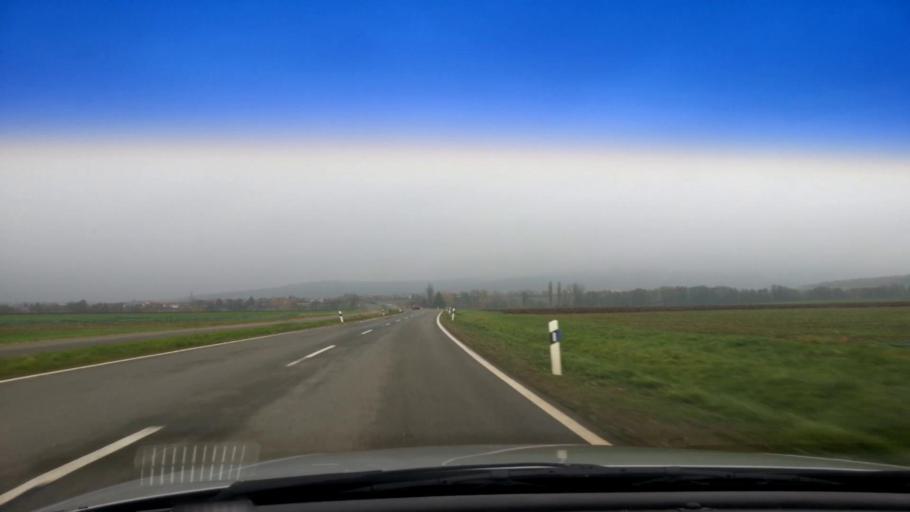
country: DE
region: Bavaria
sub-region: Upper Franconia
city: Litzendorf
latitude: 49.8996
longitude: 11.0095
